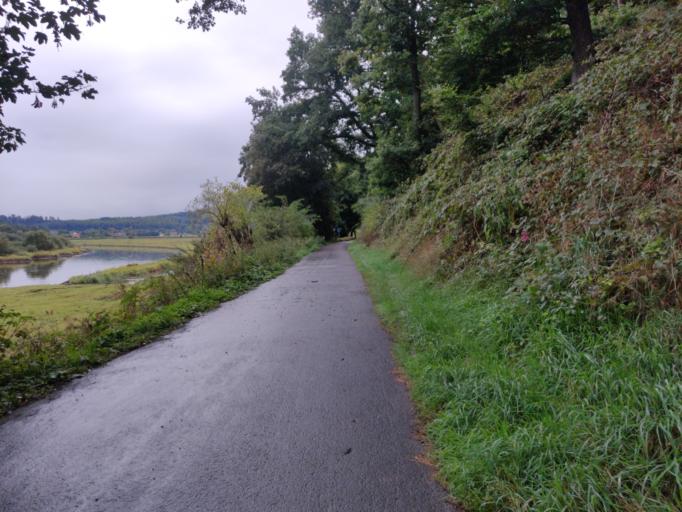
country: DE
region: Lower Saxony
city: Furstenberg
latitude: 51.7248
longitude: 9.3883
